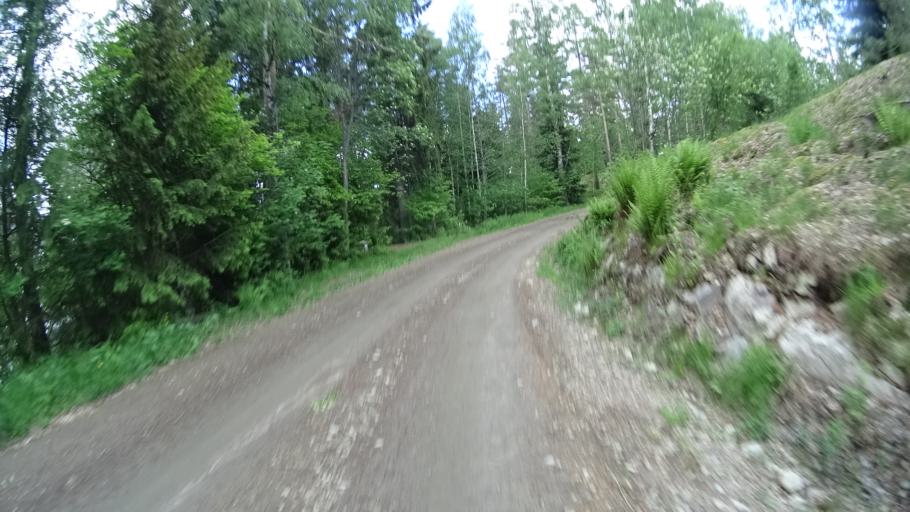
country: FI
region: Uusimaa
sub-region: Raaseporin
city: Karis
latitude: 60.1439
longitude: 23.6191
